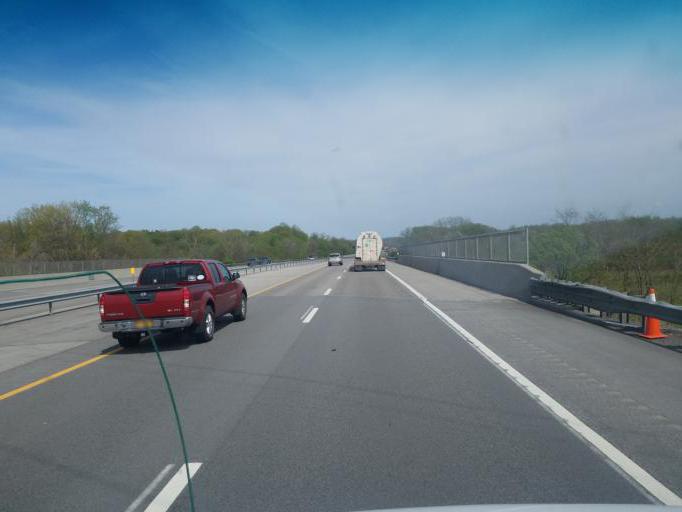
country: US
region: New York
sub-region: Monroe County
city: Scottsville
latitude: 43.0452
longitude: -77.7485
